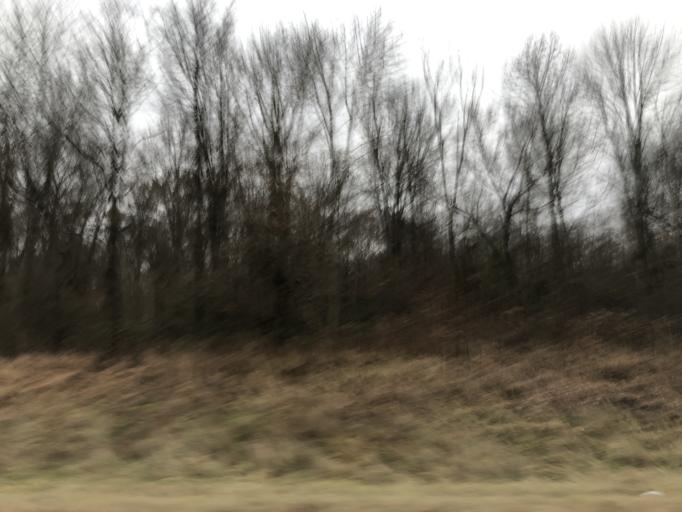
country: US
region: Illinois
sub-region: Johnson County
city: Vienna
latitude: 37.3589
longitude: -88.7949
